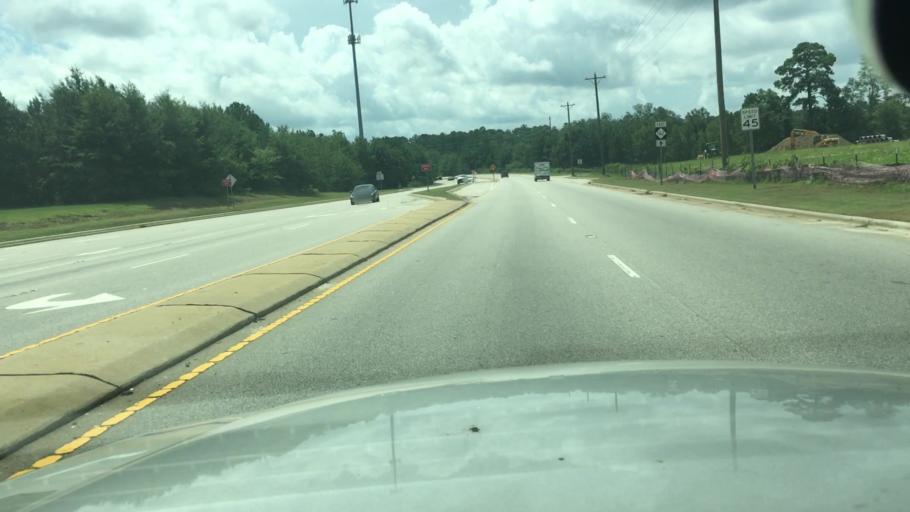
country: US
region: North Carolina
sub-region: Cumberland County
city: Hope Mills
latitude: 35.0417
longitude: -78.9902
